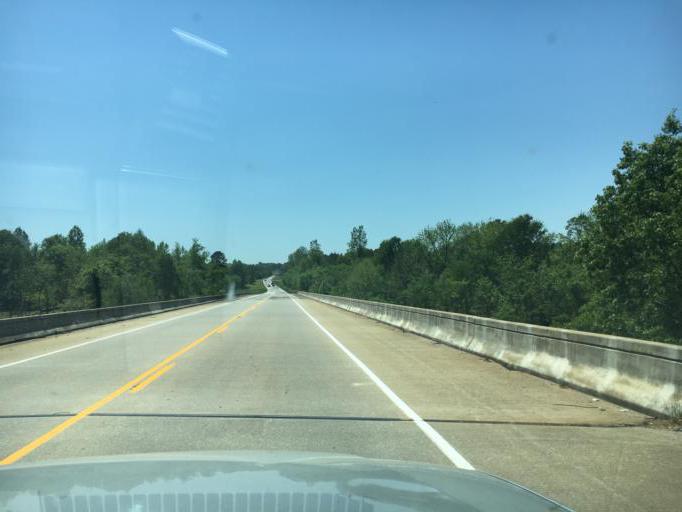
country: US
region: South Carolina
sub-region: Cherokee County
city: East Gaffney
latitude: 35.1246
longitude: -81.5868
